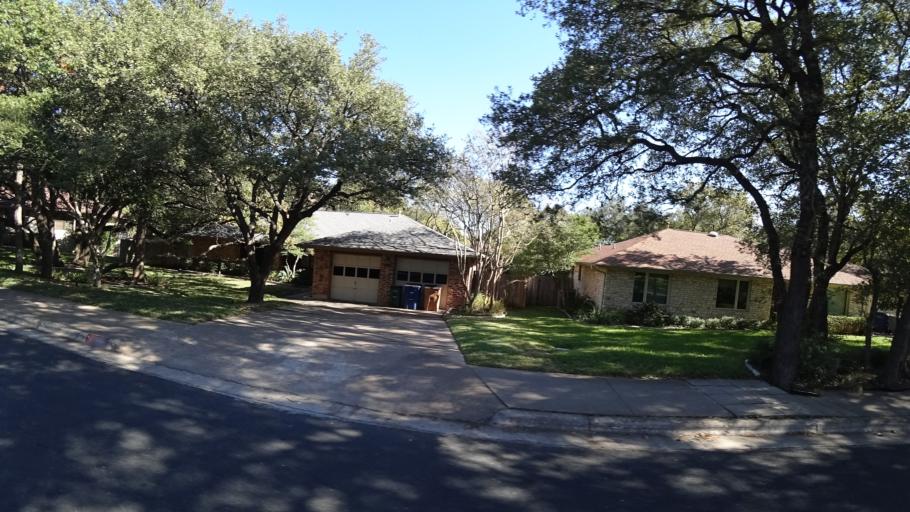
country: US
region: Texas
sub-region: Williamson County
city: Jollyville
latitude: 30.4170
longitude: -97.7688
